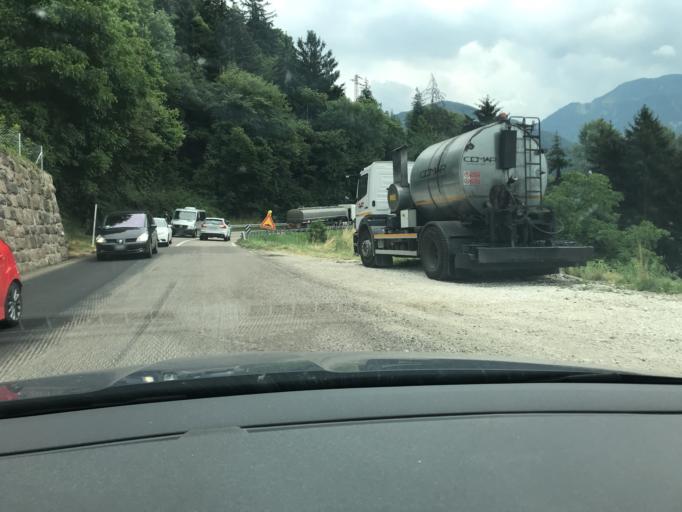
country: IT
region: Trentino-Alto Adige
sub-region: Bolzano
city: Laion
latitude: 46.6008
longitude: 11.5692
